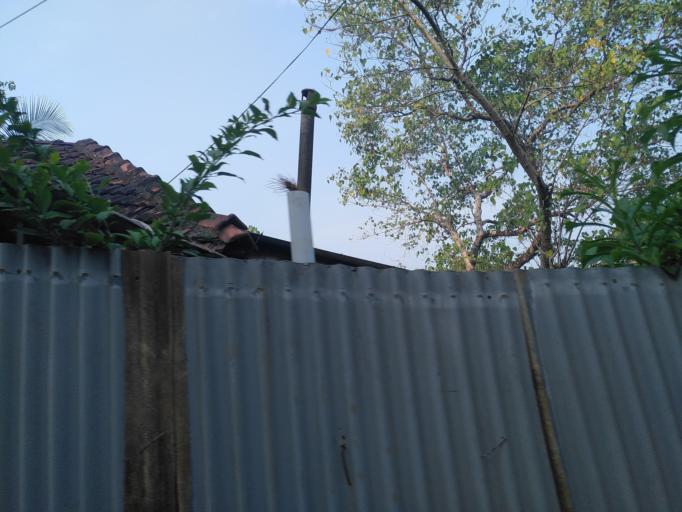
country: IN
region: Kerala
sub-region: Alappuzha
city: Arukutti
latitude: 9.9236
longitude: 76.3293
